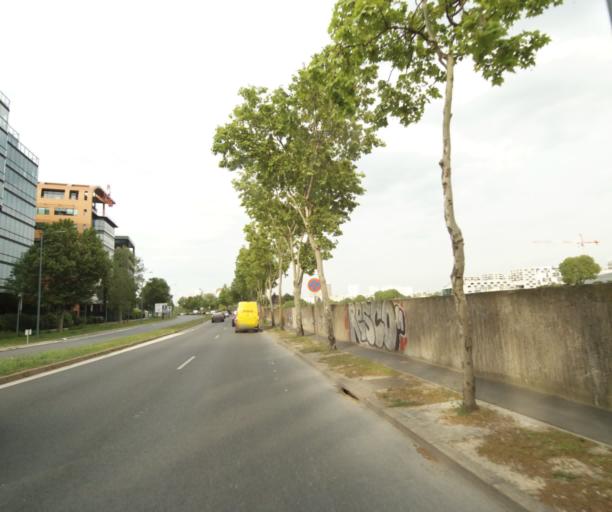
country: FR
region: Ile-de-France
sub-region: Departement des Hauts-de-Seine
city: Clichy
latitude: 48.9159
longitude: 2.3170
